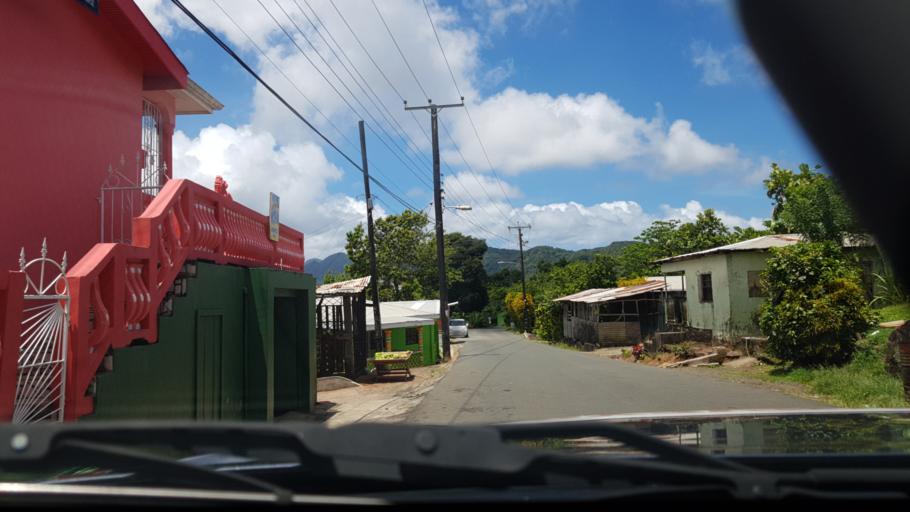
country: LC
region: Anse-la-Raye
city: Anse La Raye
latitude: 13.9411
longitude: -60.9801
